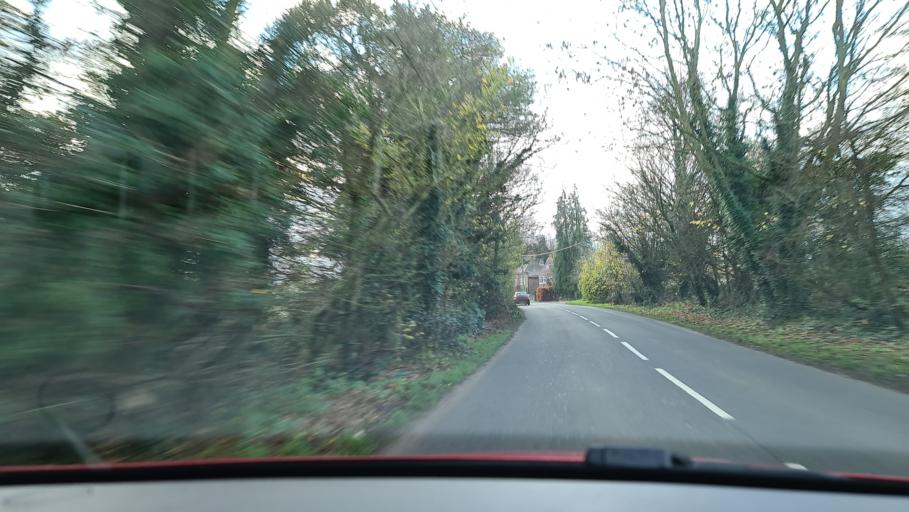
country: GB
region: England
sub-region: Buckinghamshire
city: Princes Risborough
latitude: 51.7253
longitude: -0.8487
